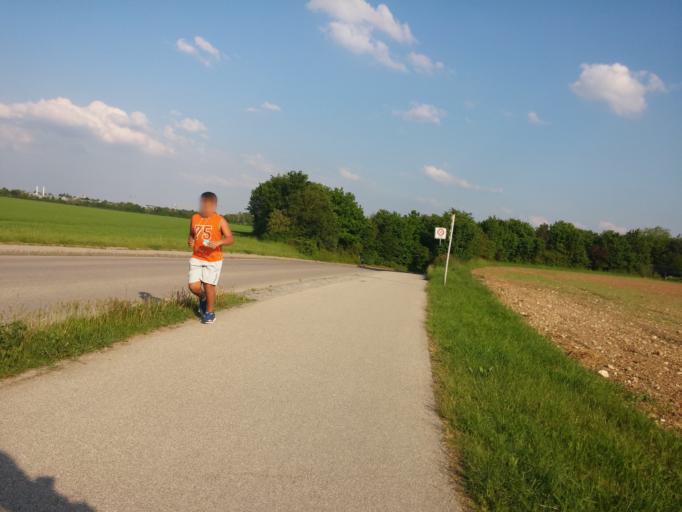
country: DE
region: Bavaria
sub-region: Upper Bavaria
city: Haar
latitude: 48.1159
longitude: 11.7147
